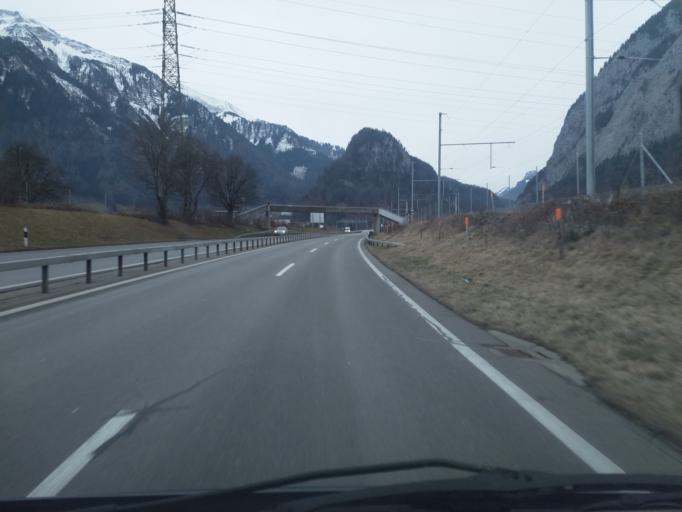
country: CH
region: Bern
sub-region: Frutigen-Niedersimmental District
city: Wimmis
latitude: 46.6848
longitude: 7.6435
